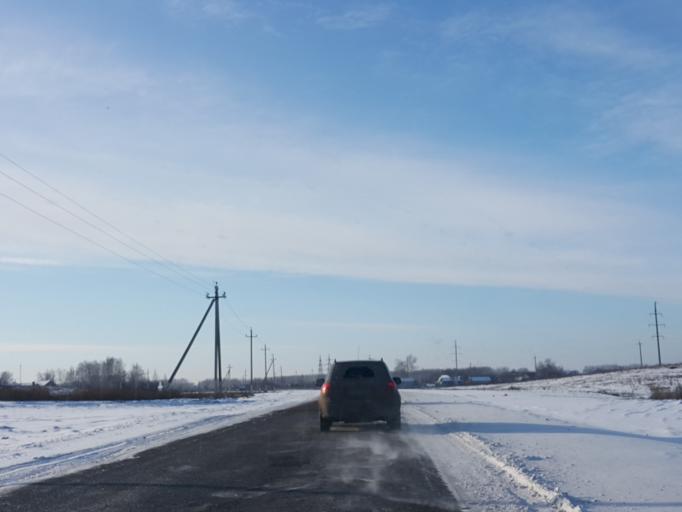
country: RU
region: Tambov
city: Znamenka
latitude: 52.4089
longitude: 41.4688
